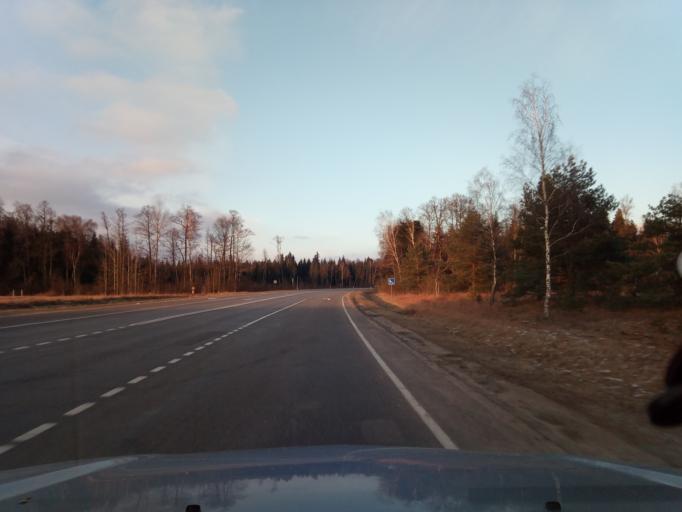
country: LT
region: Vilnius County
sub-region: Trakai
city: Rudiskes
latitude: 54.4264
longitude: 24.9792
